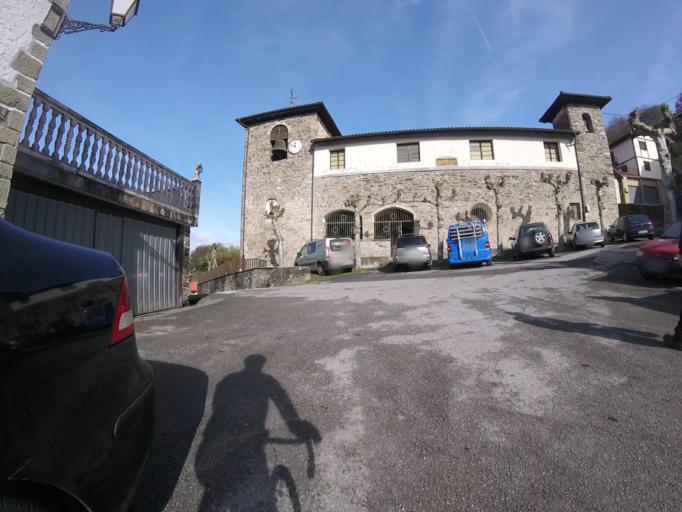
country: ES
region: Navarre
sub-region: Provincia de Navarra
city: Arano
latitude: 43.1993
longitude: -1.8947
